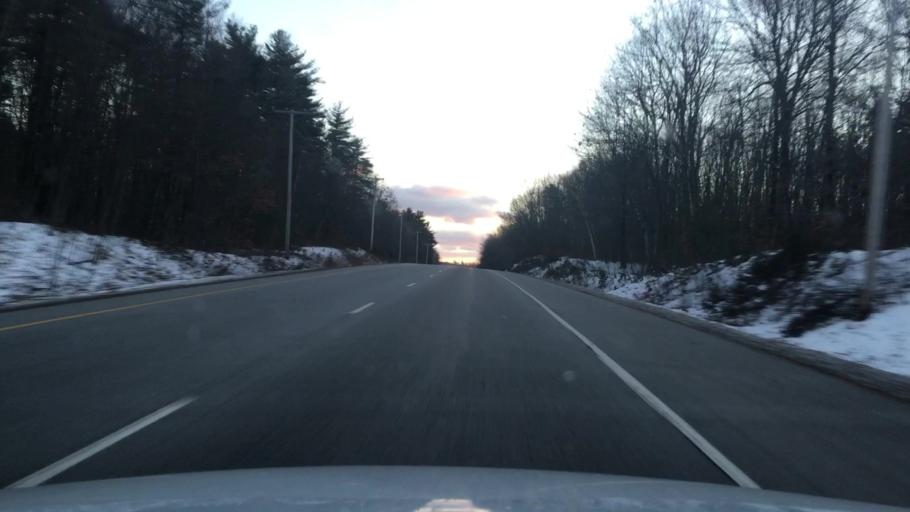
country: US
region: Maine
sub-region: Androscoggin County
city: Auburn
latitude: 44.0565
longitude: -70.2564
